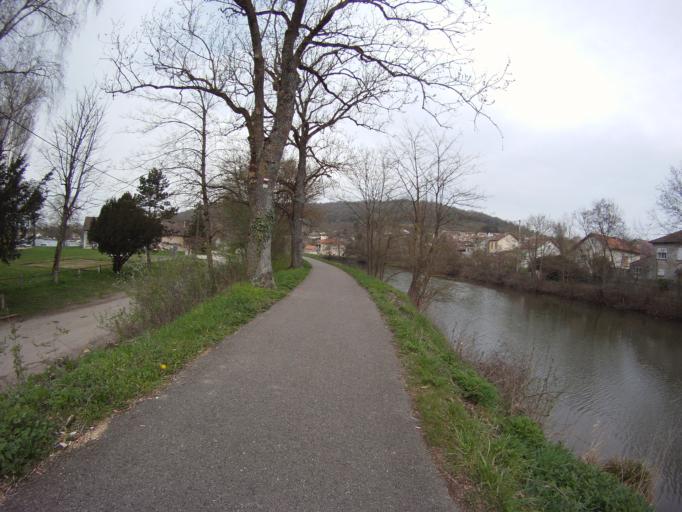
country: FR
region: Lorraine
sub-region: Departement de Meurthe-et-Moselle
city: Messein
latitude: 48.6081
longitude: 6.1490
